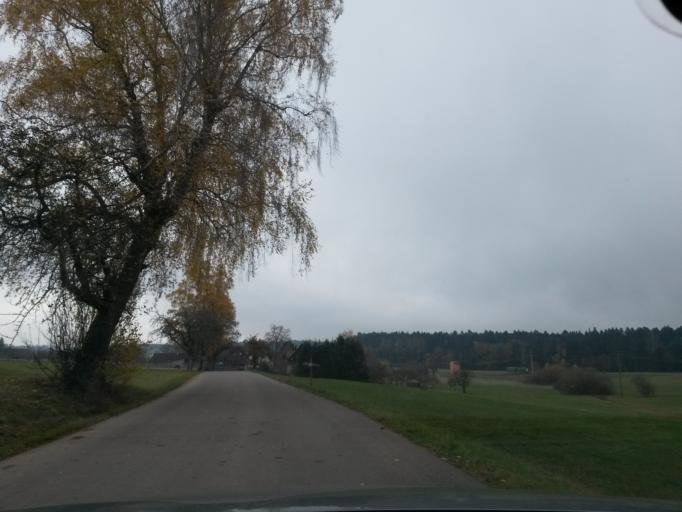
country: DE
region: Baden-Wuerttemberg
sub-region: Karlsruhe Region
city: Lossburg
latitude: 48.3783
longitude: 8.4465
